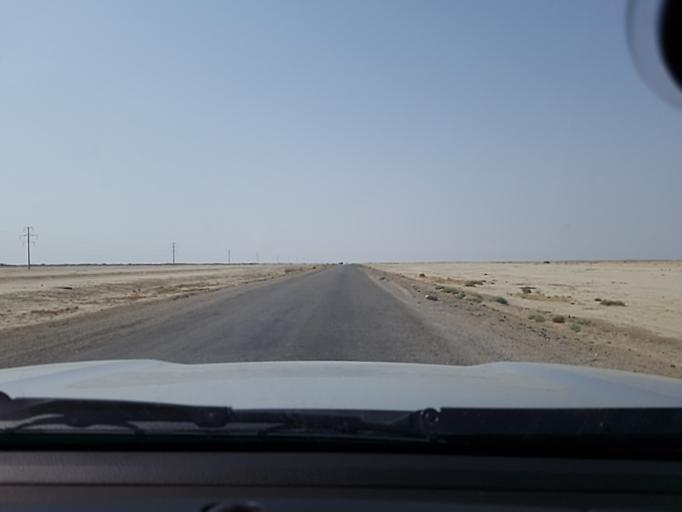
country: TM
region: Balkan
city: Gumdag
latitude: 38.8421
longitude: 54.5959
